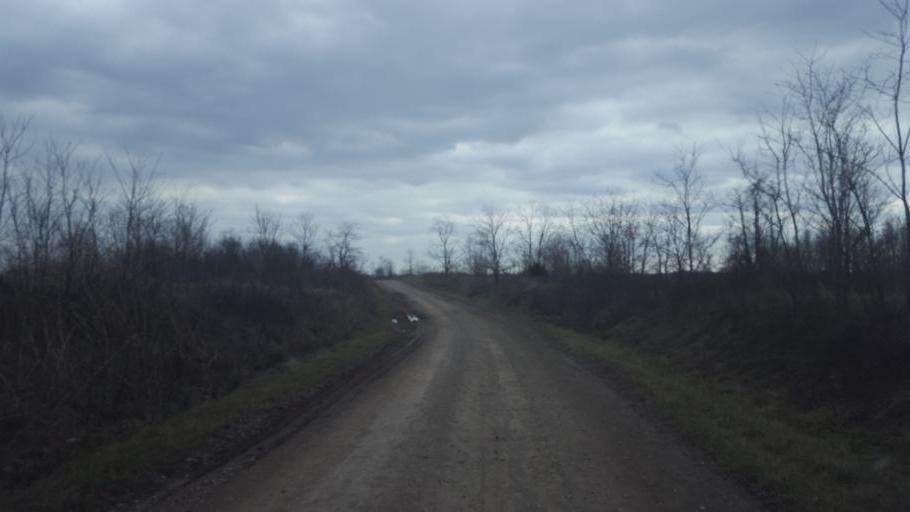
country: US
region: Ohio
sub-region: Gallia County
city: Gallipolis
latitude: 38.7367
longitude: -82.3298
